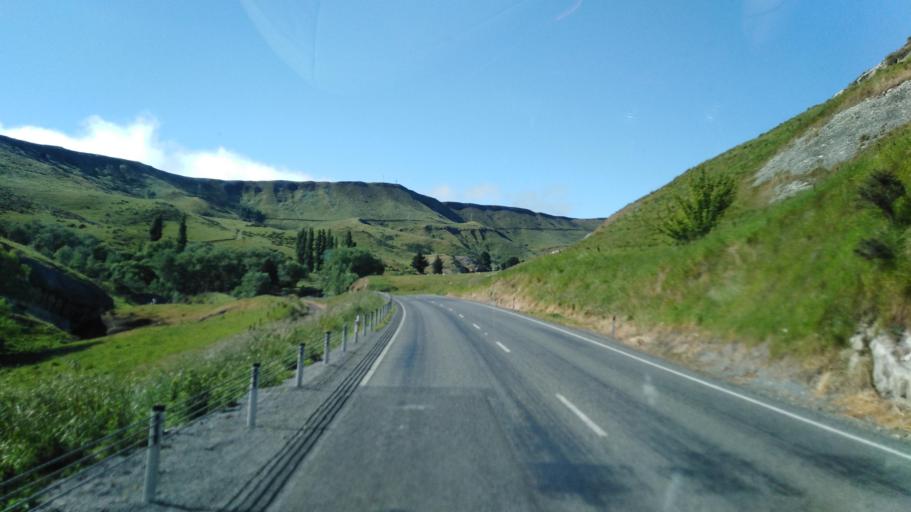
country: NZ
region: Canterbury
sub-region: Hurunui District
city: Amberley
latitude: -42.9839
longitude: 172.7186
